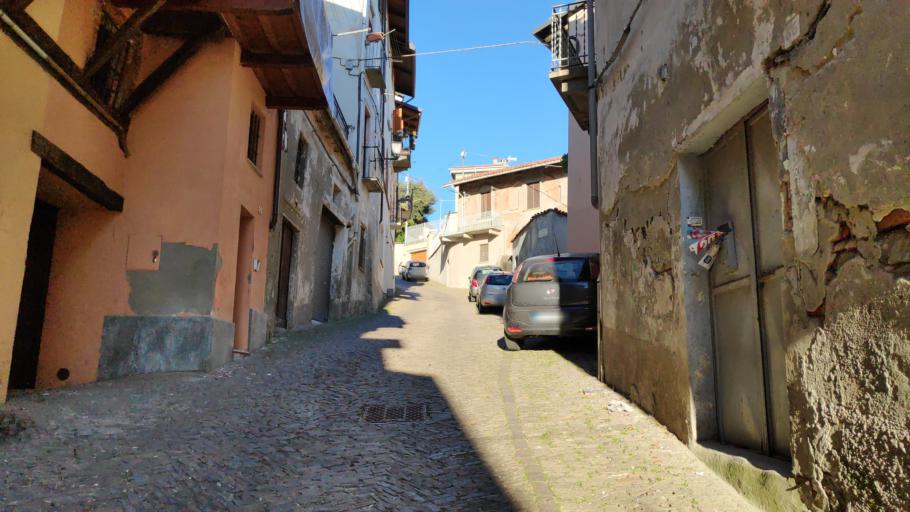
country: IT
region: Piedmont
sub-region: Provincia di Torino
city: Pinerolo
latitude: 44.8869
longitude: 7.3272
